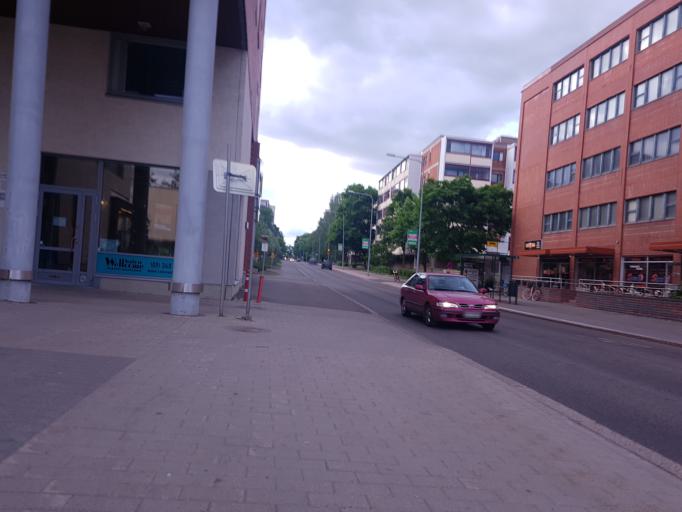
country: FI
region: Uusimaa
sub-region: Helsinki
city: Vantaa
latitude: 60.2436
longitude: 24.9940
